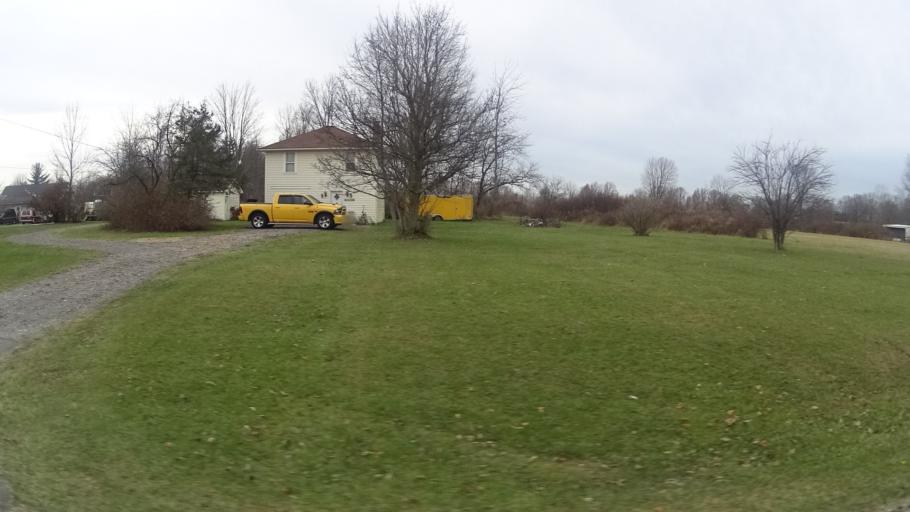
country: US
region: Ohio
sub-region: Lorain County
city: Eaton Estates
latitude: 41.3082
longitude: -81.9487
